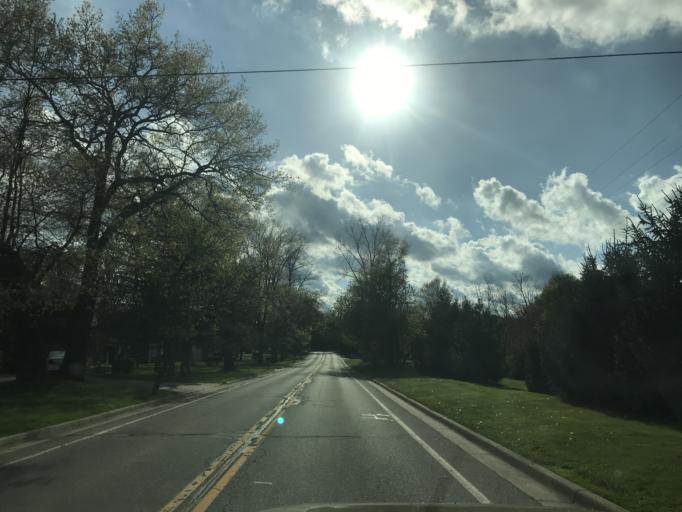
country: US
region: Michigan
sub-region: Livingston County
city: Brighton
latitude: 42.5453
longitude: -83.7448
